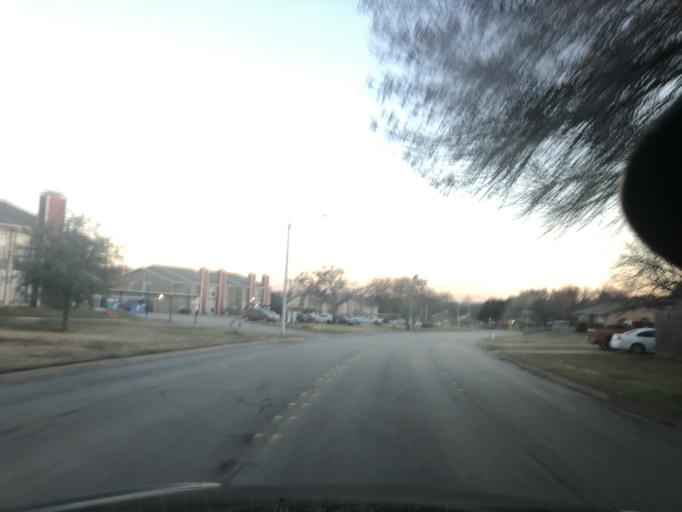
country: US
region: Texas
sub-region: Tarrant County
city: White Settlement
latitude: 32.7343
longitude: -97.4729
